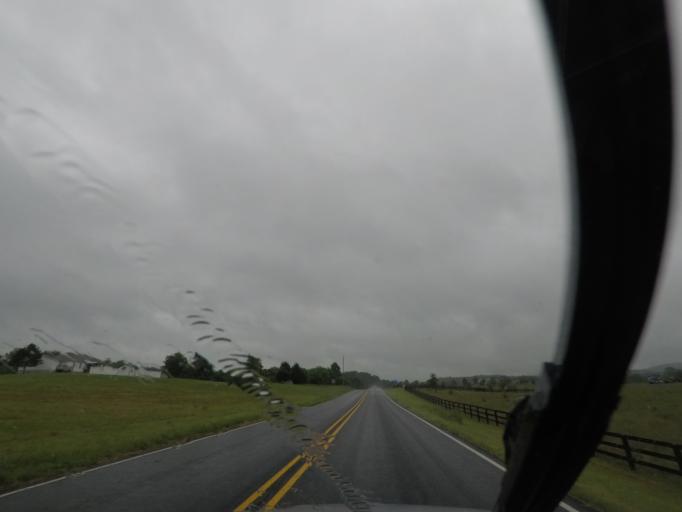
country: US
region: Virginia
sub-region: Culpeper County
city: Merrimac
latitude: 38.3565
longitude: -78.1110
